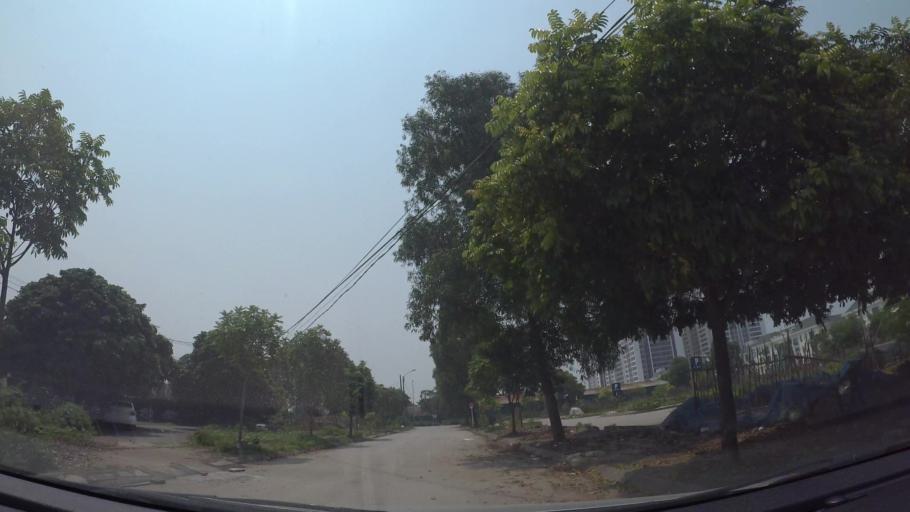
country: VN
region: Ha Noi
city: Thanh Xuan
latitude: 20.9980
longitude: 105.7856
